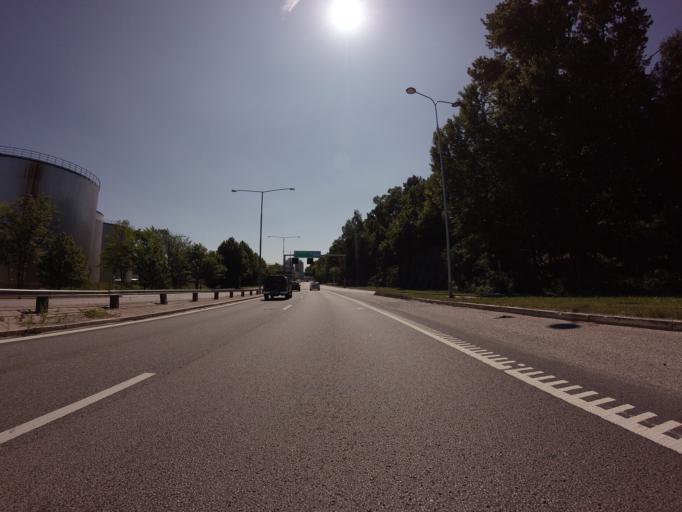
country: SE
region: Stockholm
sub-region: Stockholms Kommun
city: OEstermalm
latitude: 59.3563
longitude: 18.1042
